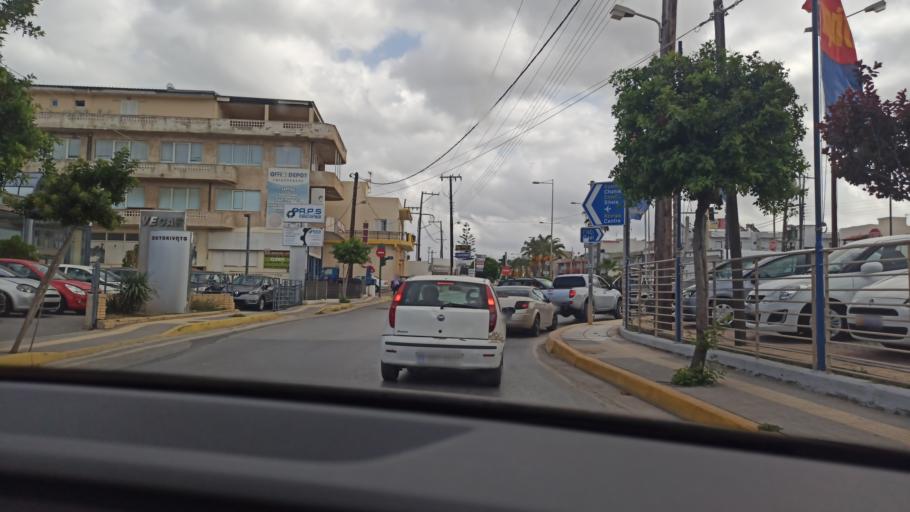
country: GR
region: Crete
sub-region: Nomos Irakleiou
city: Gazi
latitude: 35.3336
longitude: 25.0966
